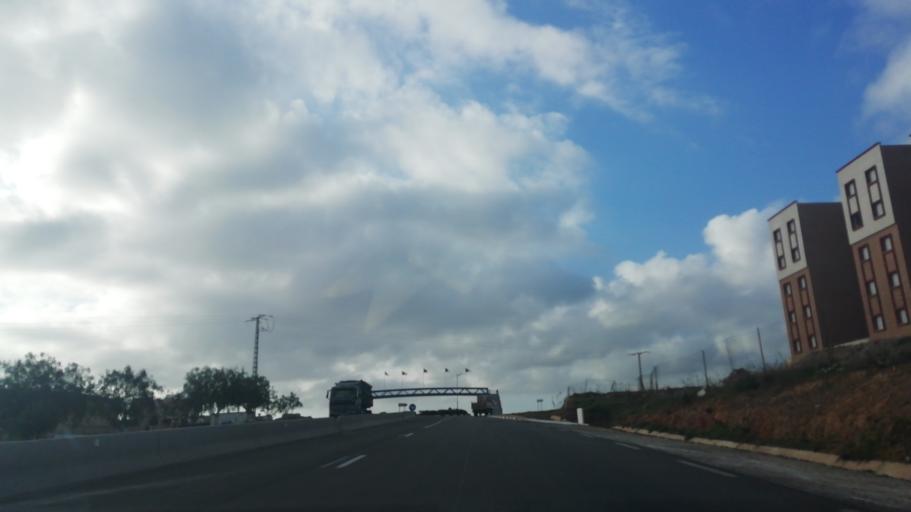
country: DZ
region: Mostaganem
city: Mostaganem
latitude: 36.1065
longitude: 0.2646
